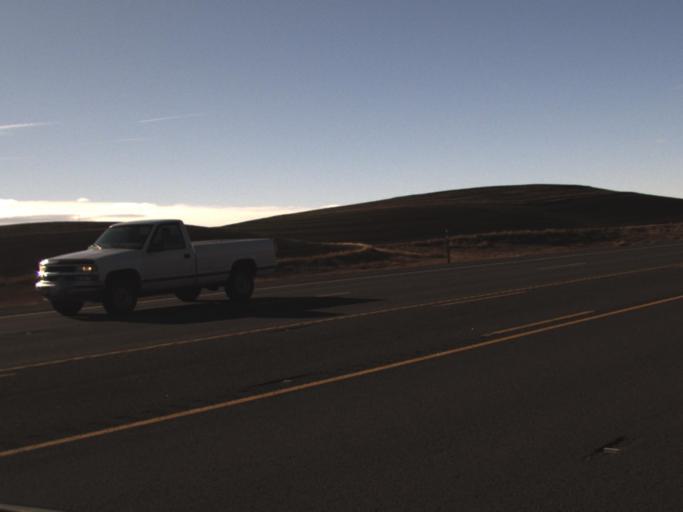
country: US
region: Idaho
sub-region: Latah County
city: Moscow
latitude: 46.7343
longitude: -117.0777
